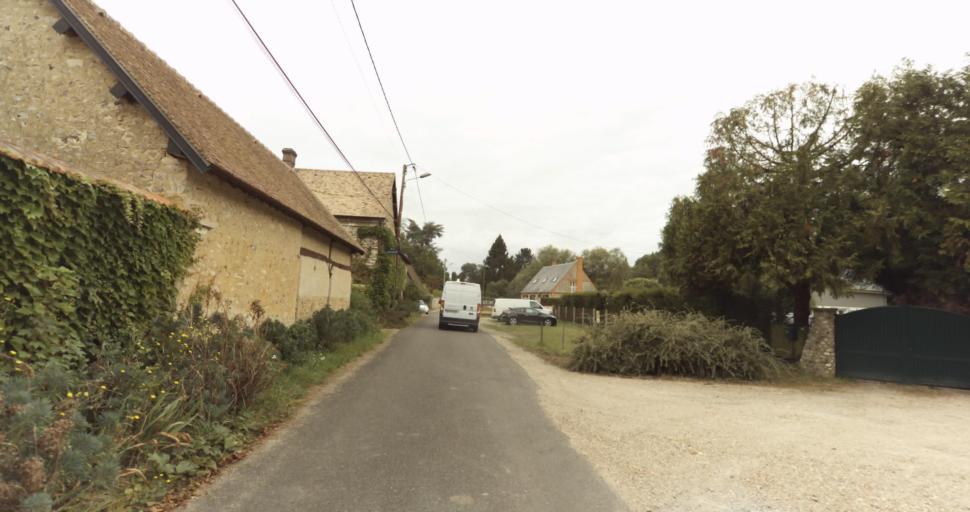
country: FR
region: Haute-Normandie
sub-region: Departement de l'Eure
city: Houlbec-Cocherel
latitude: 49.0774
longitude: 1.2853
